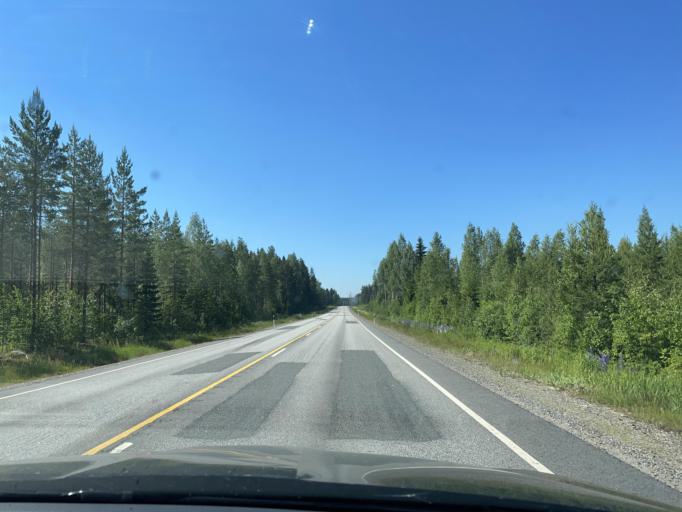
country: FI
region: Central Finland
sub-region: Saarijaervi-Viitasaari
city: Viitasaari
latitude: 63.1756
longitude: 26.0228
